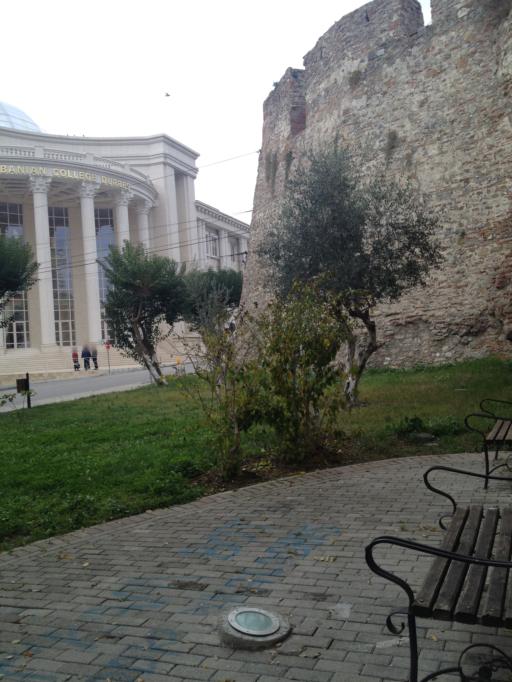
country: AL
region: Durres
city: Durres
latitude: 41.3105
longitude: 19.4457
